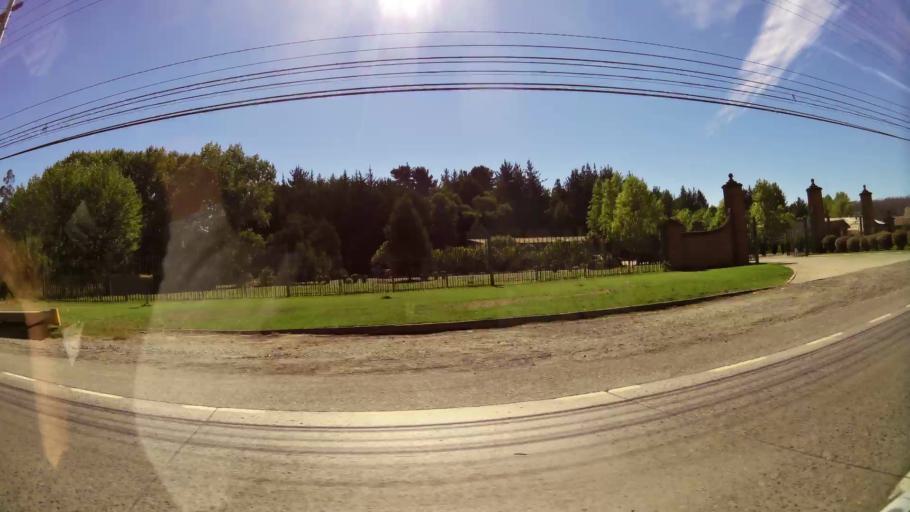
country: CL
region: Biobio
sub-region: Provincia de Concepcion
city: Penco
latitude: -36.7740
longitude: -73.0160
